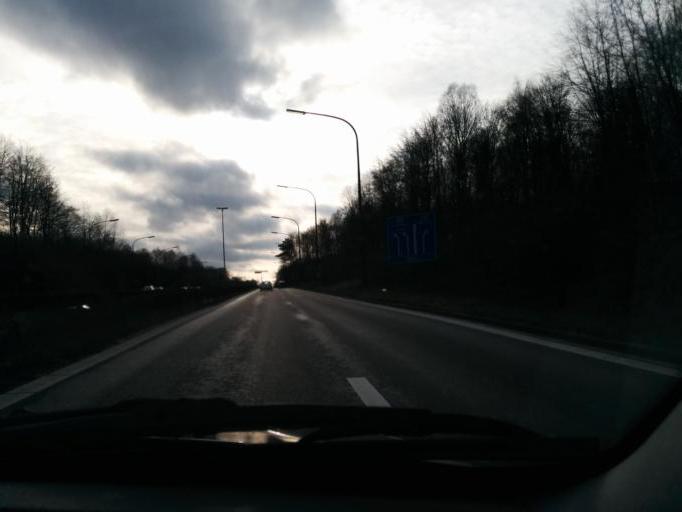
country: BE
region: Flanders
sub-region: Provincie Vlaams-Brabant
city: Hoeilaart
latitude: 50.8040
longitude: 4.4666
